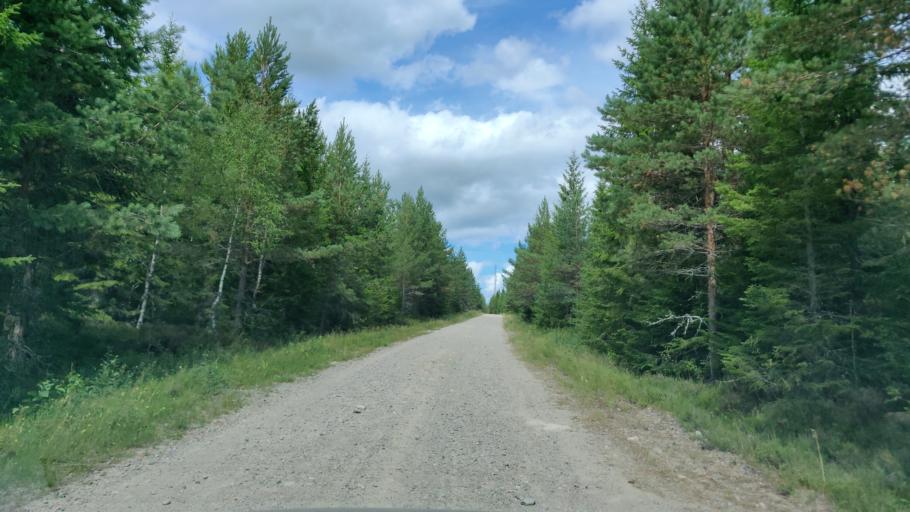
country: SE
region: Vaermland
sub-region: Hagfors Kommun
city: Hagfors
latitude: 60.0113
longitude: 13.7277
